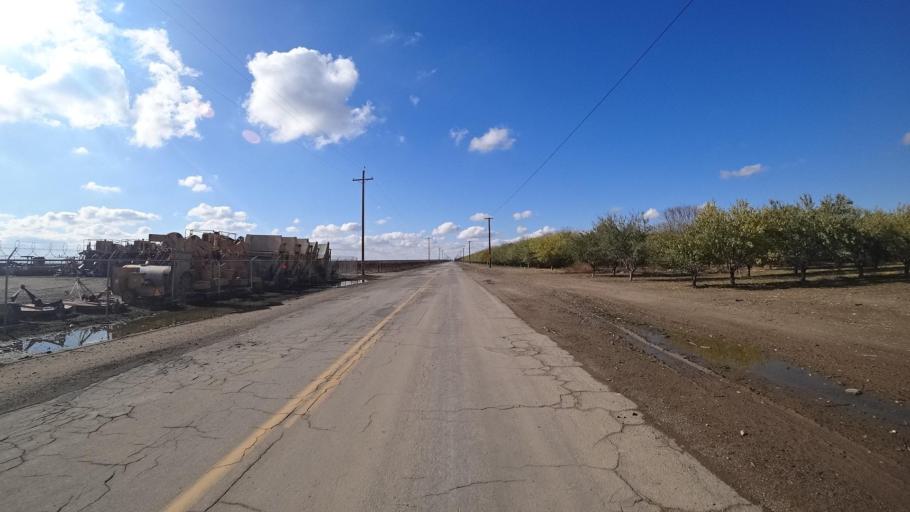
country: US
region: California
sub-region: Kern County
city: Wasco
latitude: 35.7031
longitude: -119.3666
